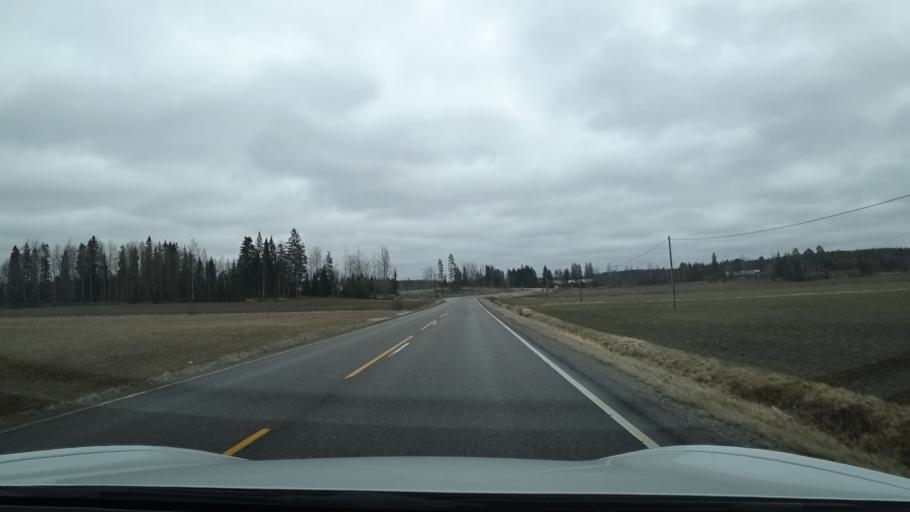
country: FI
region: Uusimaa
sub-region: Helsinki
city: Pornainen
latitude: 60.4862
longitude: 25.4455
